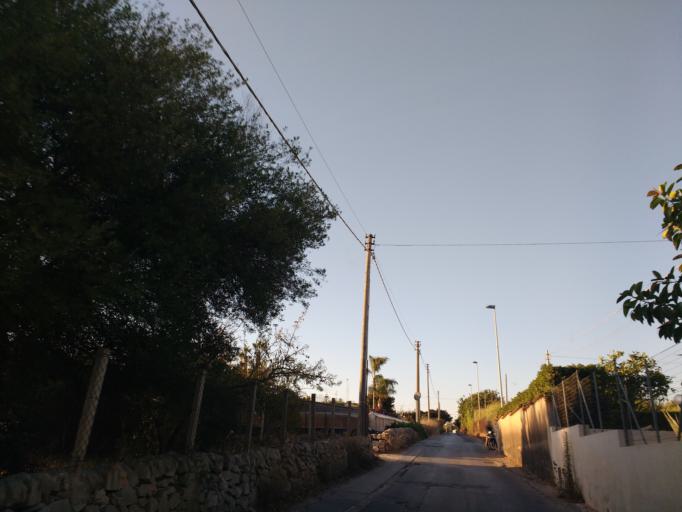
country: IT
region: Sicily
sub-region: Ragusa
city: Cava d'Aliga
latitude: 36.7249
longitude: 14.6967
